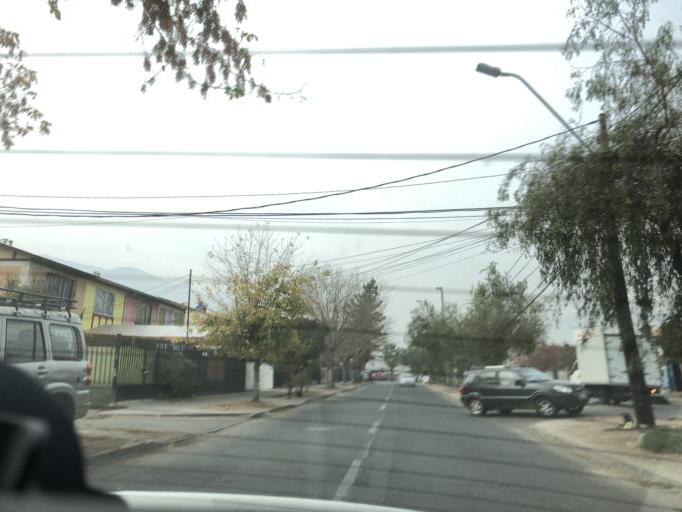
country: CL
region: Santiago Metropolitan
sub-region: Provincia de Cordillera
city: Puente Alto
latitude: -33.5925
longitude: -70.5615
